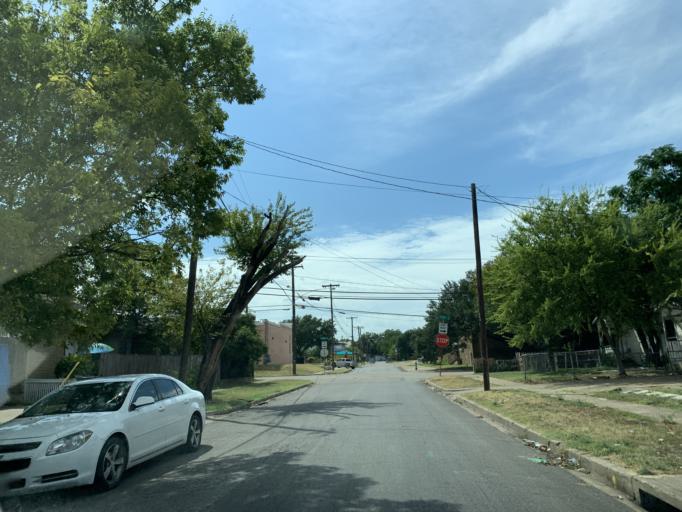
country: US
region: Texas
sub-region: Dallas County
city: Cockrell Hill
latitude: 32.7402
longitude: -96.8370
